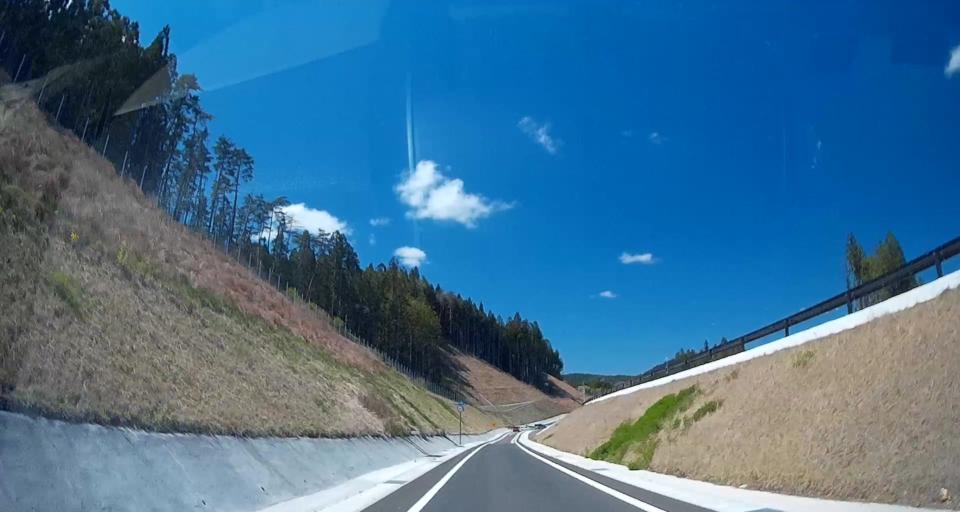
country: JP
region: Iwate
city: Ofunato
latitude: 38.9843
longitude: 141.6135
